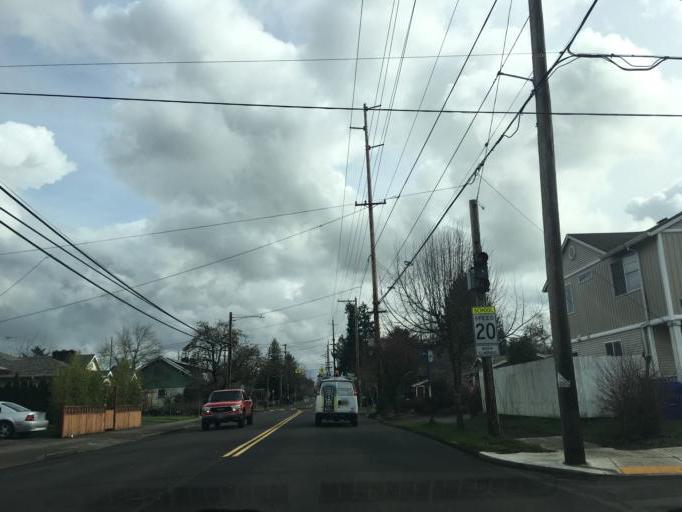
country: US
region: Oregon
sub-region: Multnomah County
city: Lents
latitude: 45.4903
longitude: -122.5846
